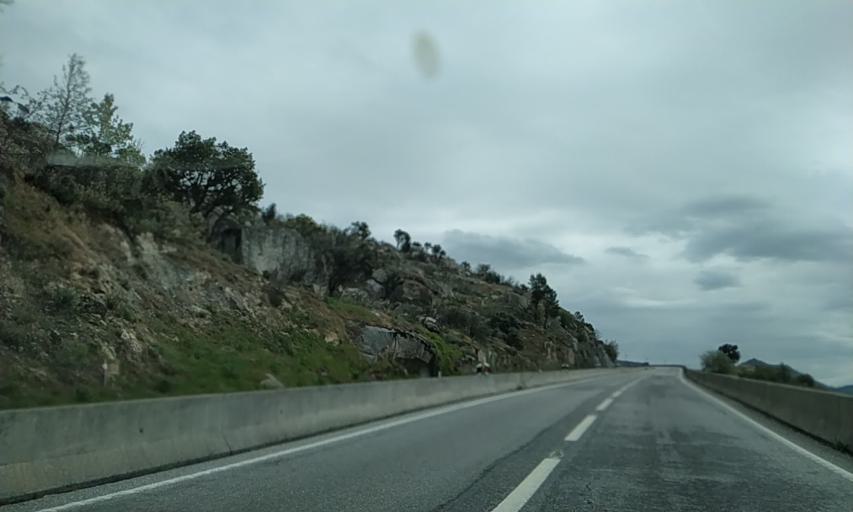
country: PT
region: Guarda
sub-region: Guarda
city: Guarda
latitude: 40.6072
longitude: -7.2829
